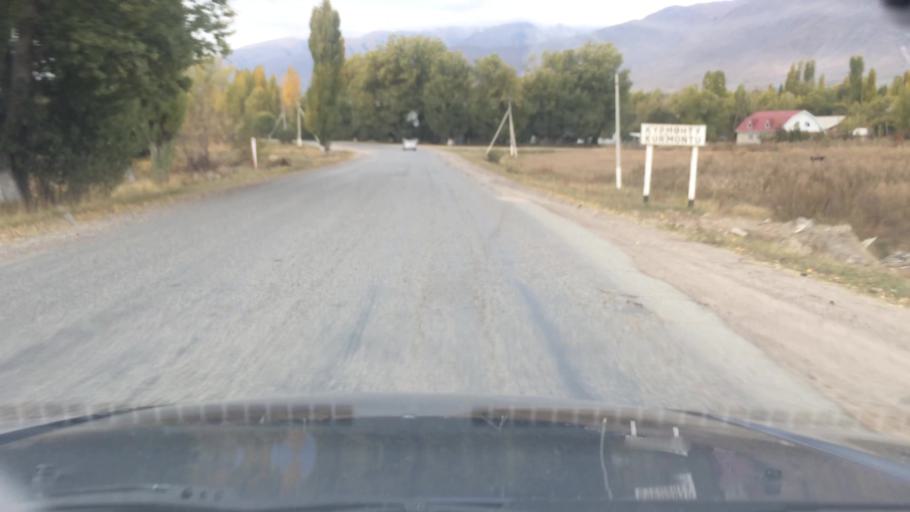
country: KG
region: Ysyk-Koel
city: Tyup
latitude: 42.7868
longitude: 78.2641
